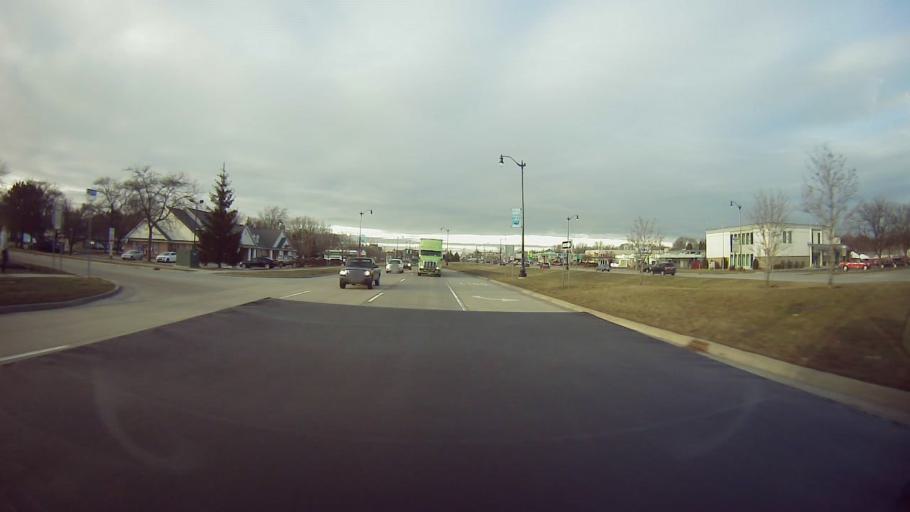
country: US
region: Michigan
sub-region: Wayne County
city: Taylor
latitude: 42.2389
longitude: -83.2698
